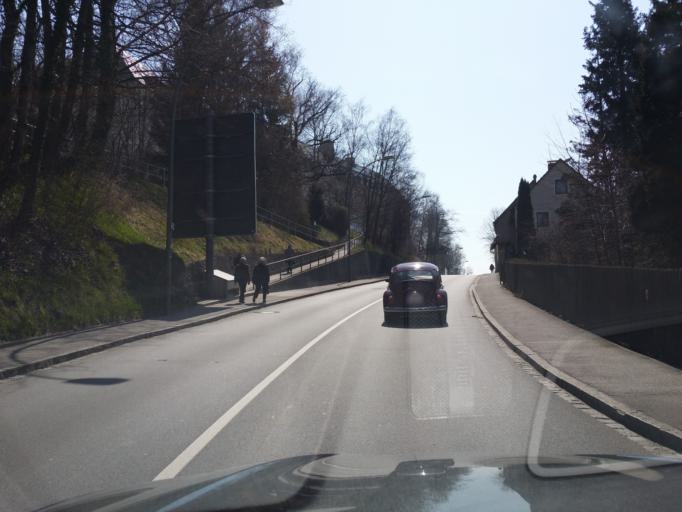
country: DE
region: Bavaria
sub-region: Lower Bavaria
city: Landshut
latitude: 48.5238
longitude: 12.1455
